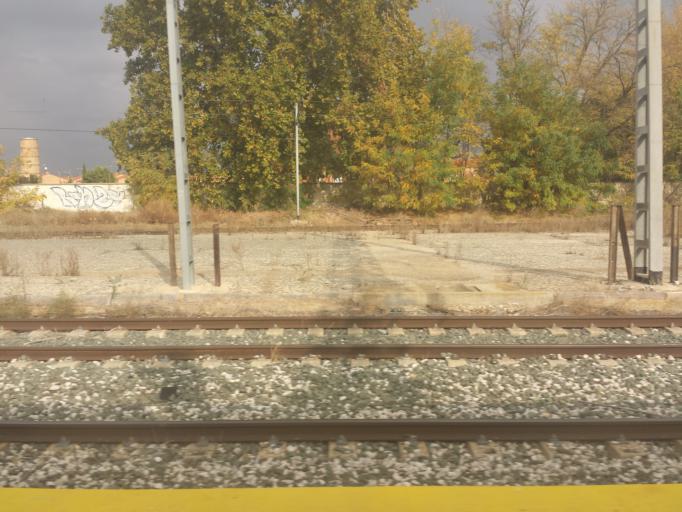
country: ES
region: Navarre
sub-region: Provincia de Navarra
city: Cortes
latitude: 41.9155
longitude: -1.4207
